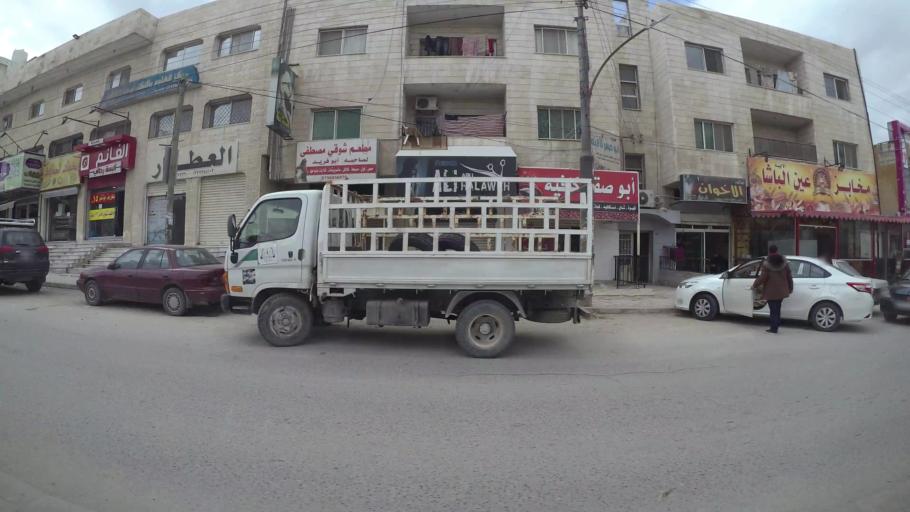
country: JO
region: Amman
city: Al Jubayhah
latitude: 32.0586
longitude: 35.8356
